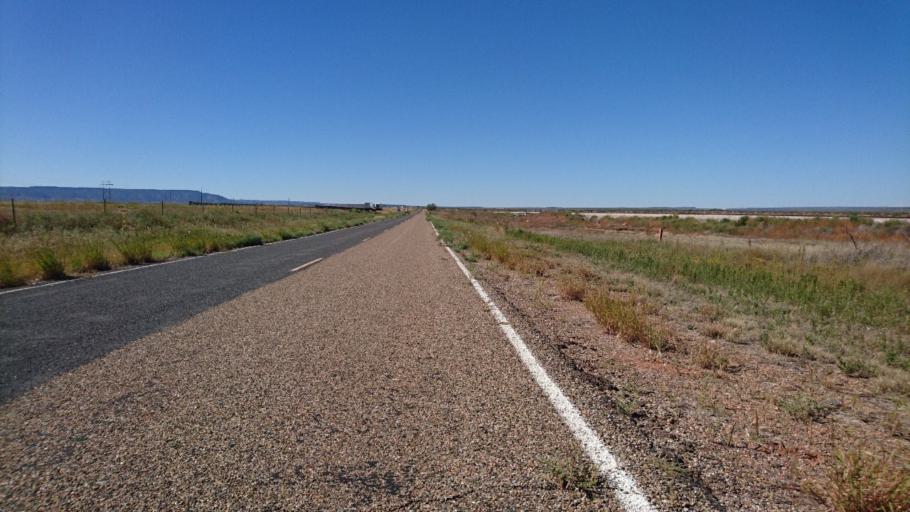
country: US
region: New Mexico
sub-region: Quay County
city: Tucumcari
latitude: 35.1040
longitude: -104.0357
